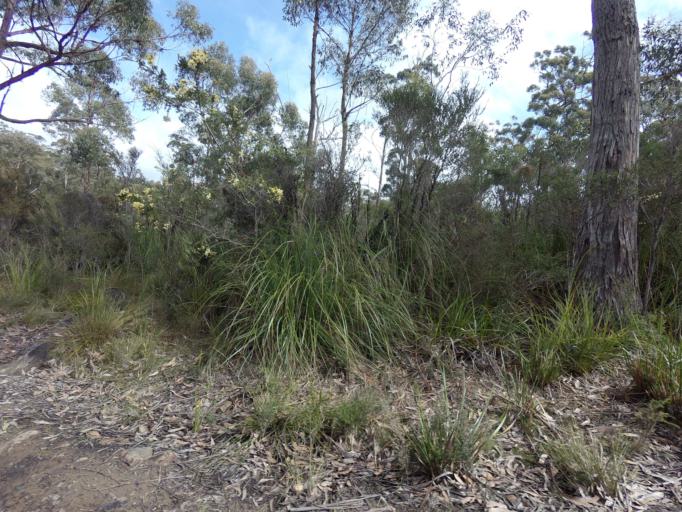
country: AU
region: Tasmania
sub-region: Huon Valley
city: Geeveston
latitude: -43.4809
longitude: 146.9383
